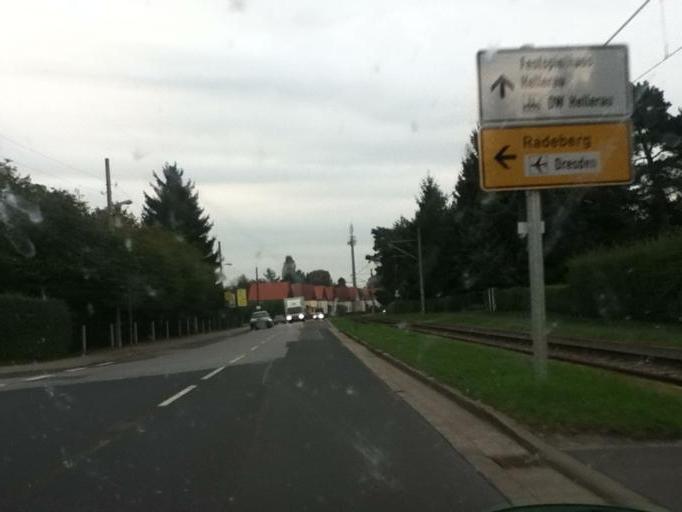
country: DE
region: Saxony
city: Albertstadt
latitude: 51.1156
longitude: 13.7462
